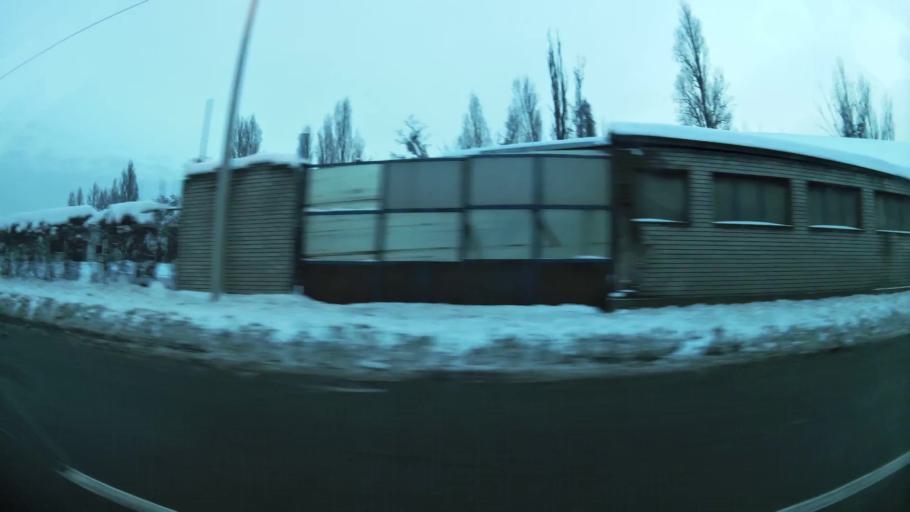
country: RS
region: Central Serbia
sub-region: Belgrade
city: Stari Grad
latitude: 44.8225
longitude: 20.4727
